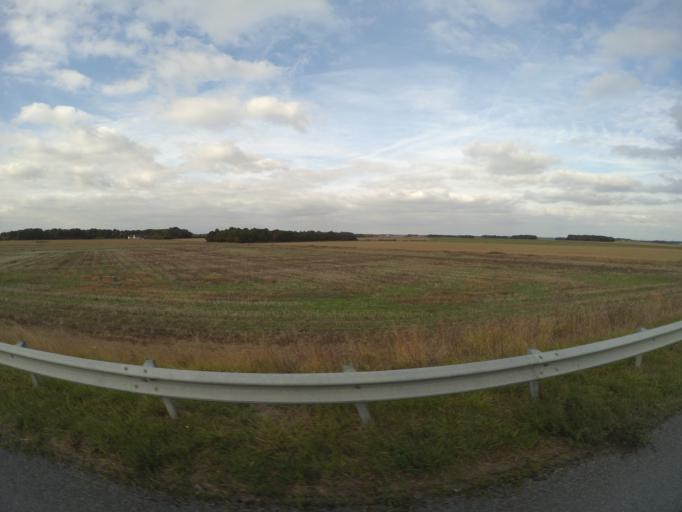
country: FR
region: Centre
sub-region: Departement d'Indre-et-Loire
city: Reugny
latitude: 47.4698
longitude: 0.9155
